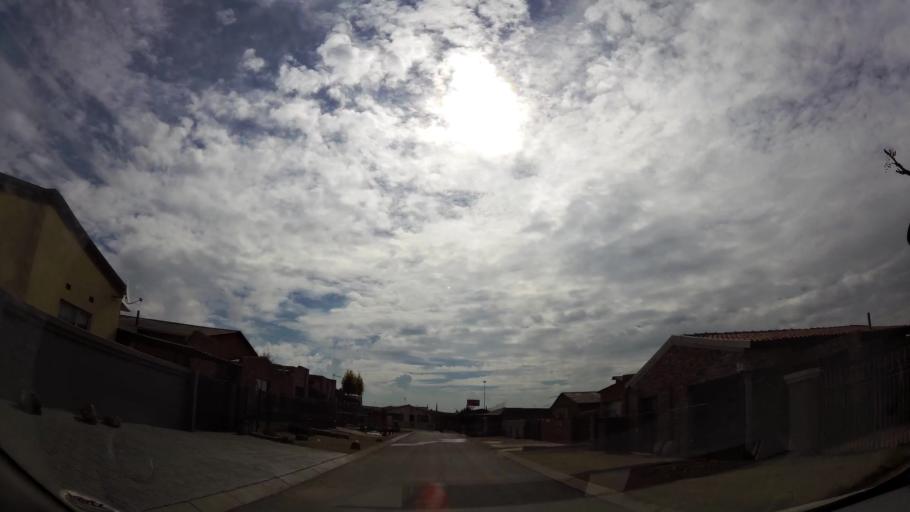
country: ZA
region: Gauteng
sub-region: Ekurhuleni Metropolitan Municipality
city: Germiston
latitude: -26.3791
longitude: 28.1675
